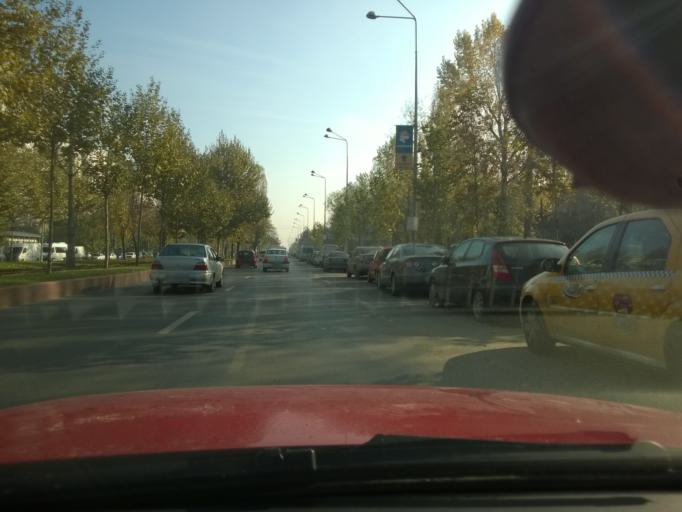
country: RO
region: Ilfov
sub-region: Comuna Popesti-Leordeni
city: Popesti-Leordeni
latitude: 44.4105
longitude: 26.1747
